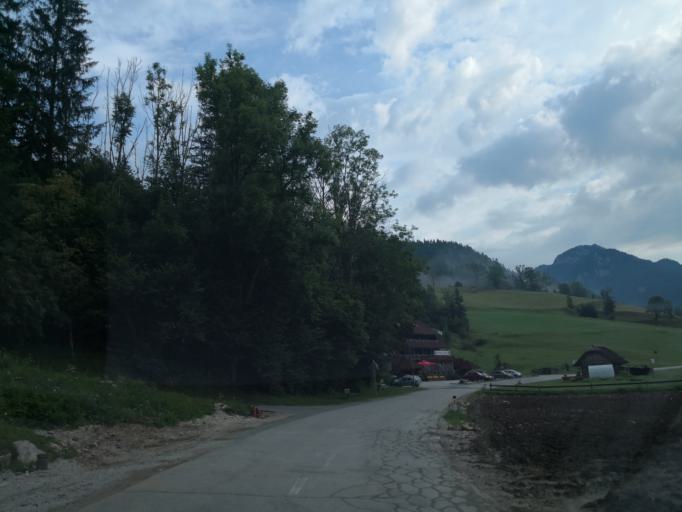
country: SI
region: Jezersko
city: Zgornje Jezersko
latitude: 46.3953
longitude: 14.5007
